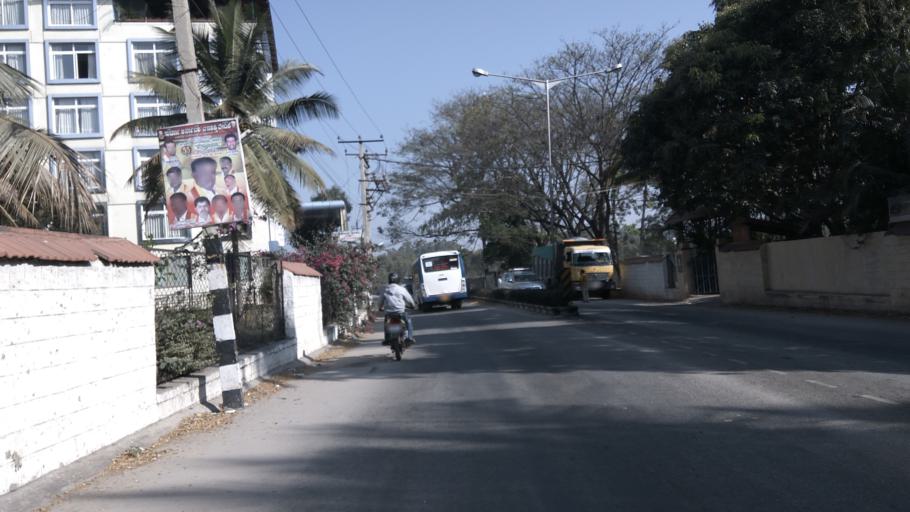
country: IN
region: Karnataka
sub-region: Bangalore Rural
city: Devanhalli
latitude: 13.1925
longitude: 77.6458
